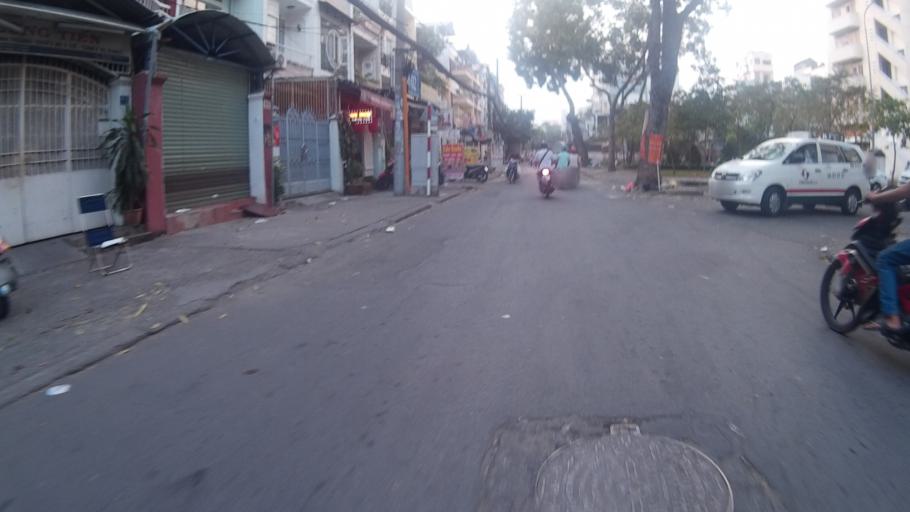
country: VN
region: Ho Chi Minh City
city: Quan Mot
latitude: 10.7900
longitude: 106.7108
